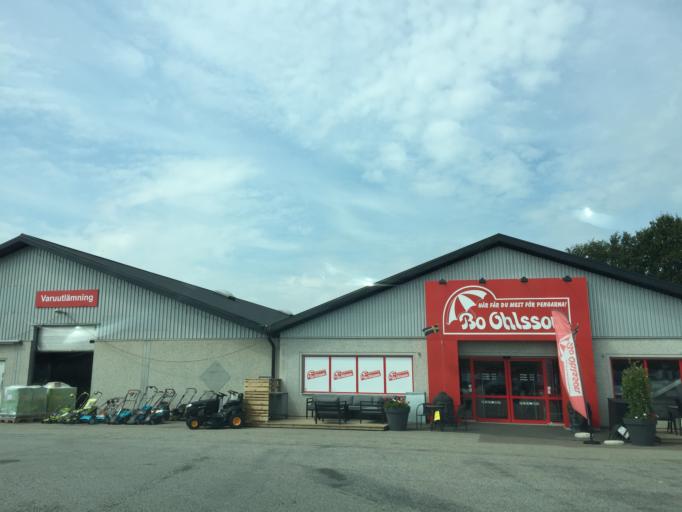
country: SE
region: Skane
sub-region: Tomelilla Kommun
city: Tomelilla
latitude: 55.5484
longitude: 13.9476
